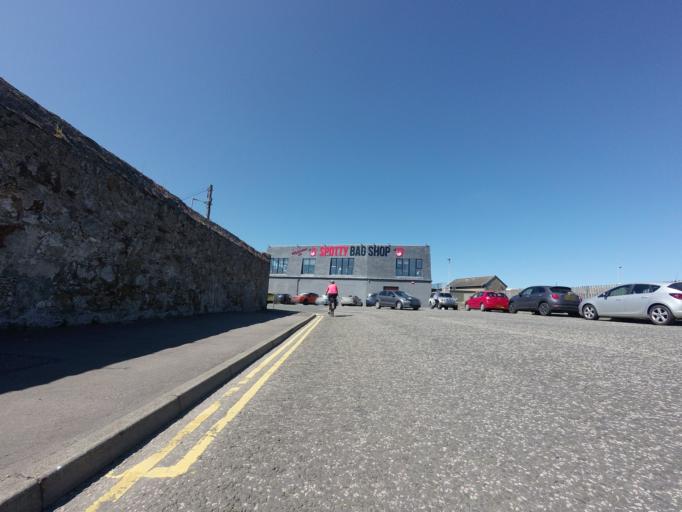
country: GB
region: Scotland
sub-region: Aberdeenshire
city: Banff
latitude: 57.6645
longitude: -2.5166
